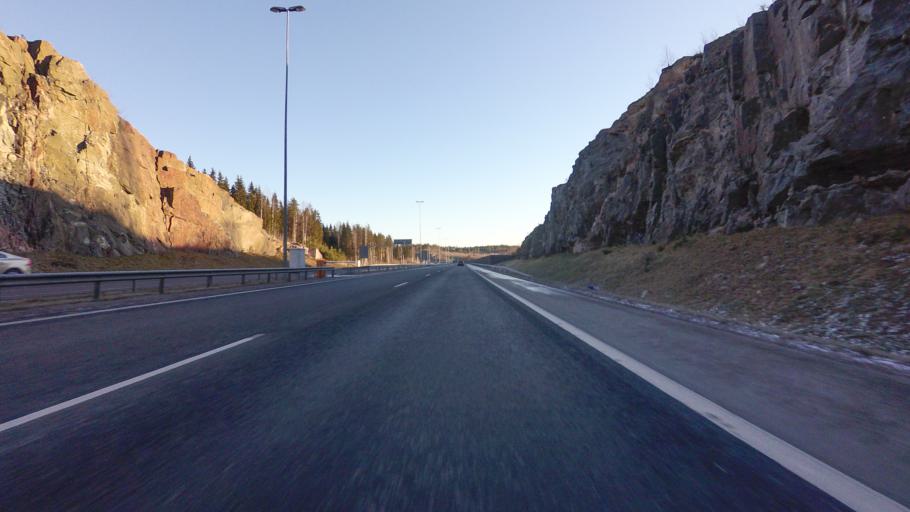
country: FI
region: Uusimaa
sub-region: Helsinki
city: Lohja
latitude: 60.2865
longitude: 24.0869
